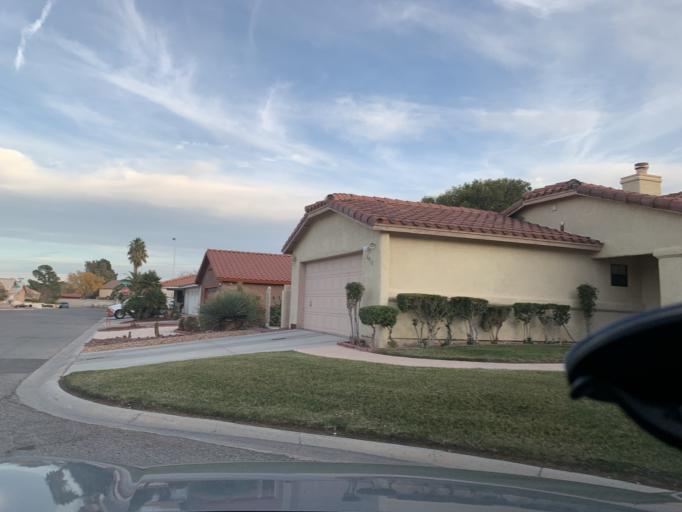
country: US
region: Nevada
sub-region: Clark County
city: Spring Valley
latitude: 36.0914
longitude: -115.2326
